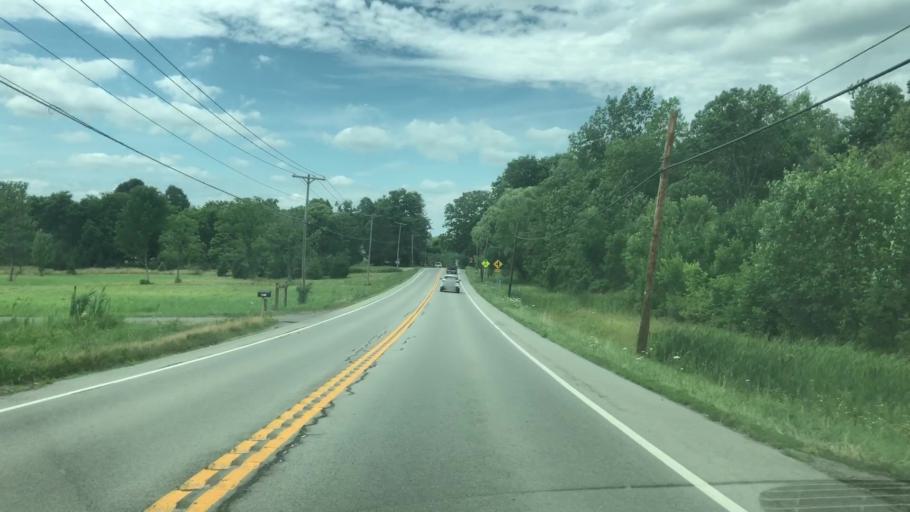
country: US
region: New York
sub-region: Monroe County
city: Fairport
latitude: 43.1307
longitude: -77.3954
